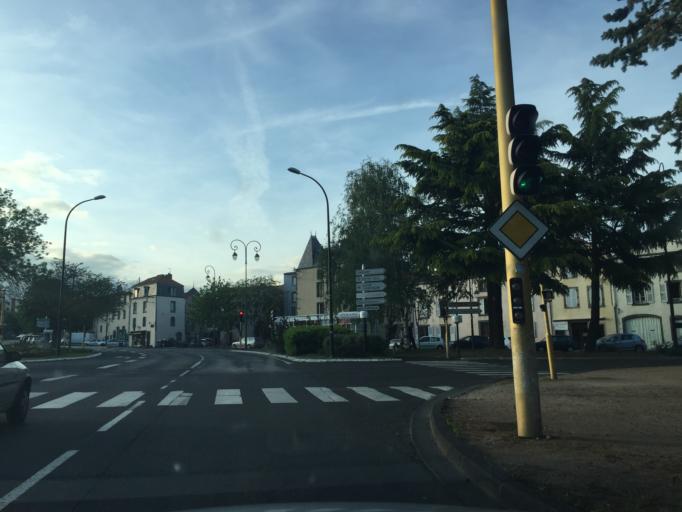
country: FR
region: Auvergne
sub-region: Departement du Puy-de-Dome
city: Riom
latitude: 45.8907
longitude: 3.1104
